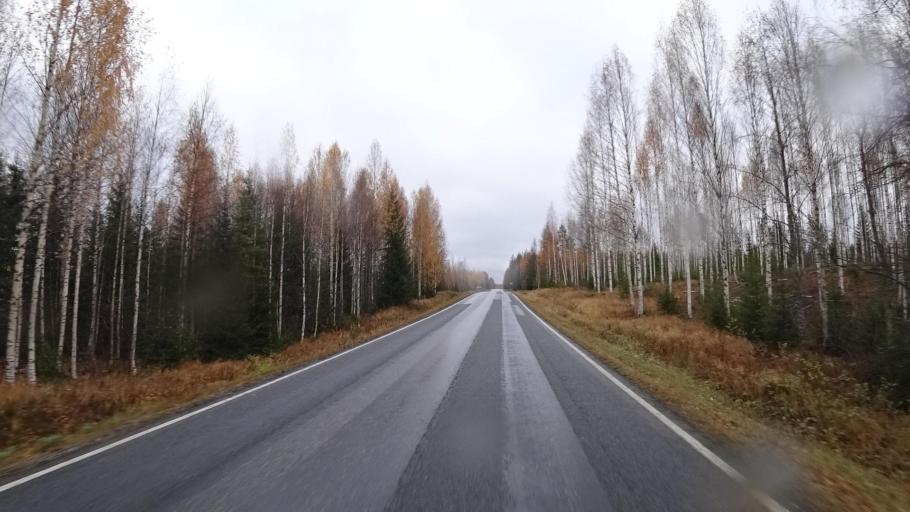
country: FI
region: North Karelia
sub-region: Joensuu
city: Polvijaervi
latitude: 63.0899
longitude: 29.5980
